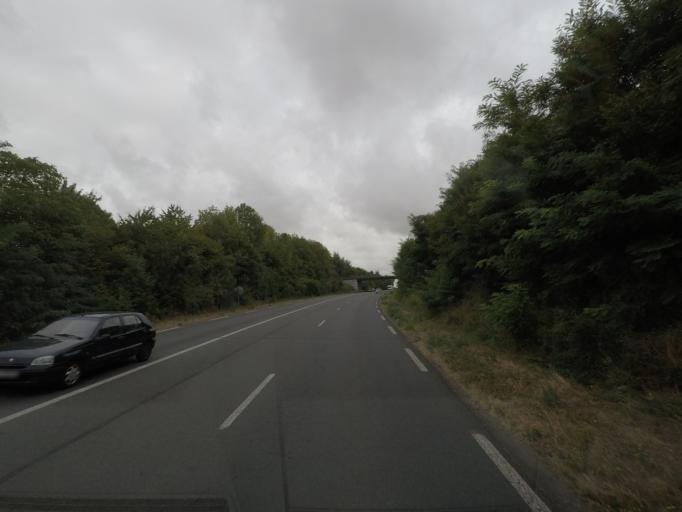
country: FR
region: Poitou-Charentes
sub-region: Departement des Deux-Sevres
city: Celles-sur-Belle
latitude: 46.2525
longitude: -0.2214
